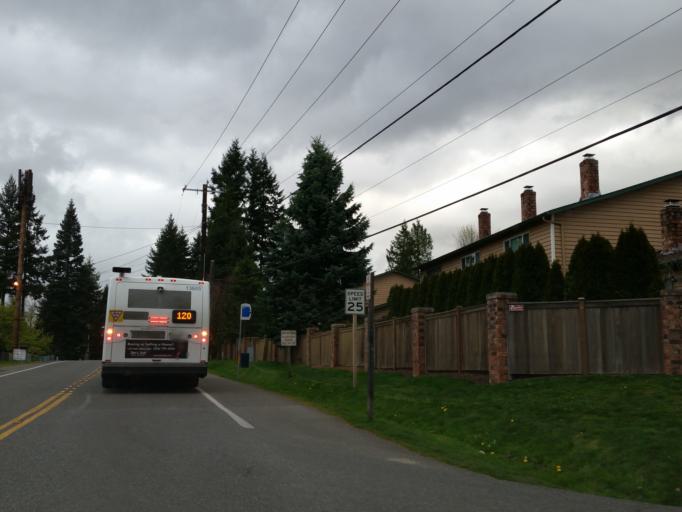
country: US
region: Washington
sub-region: Snohomish County
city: Brier
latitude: 47.8023
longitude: -122.2384
